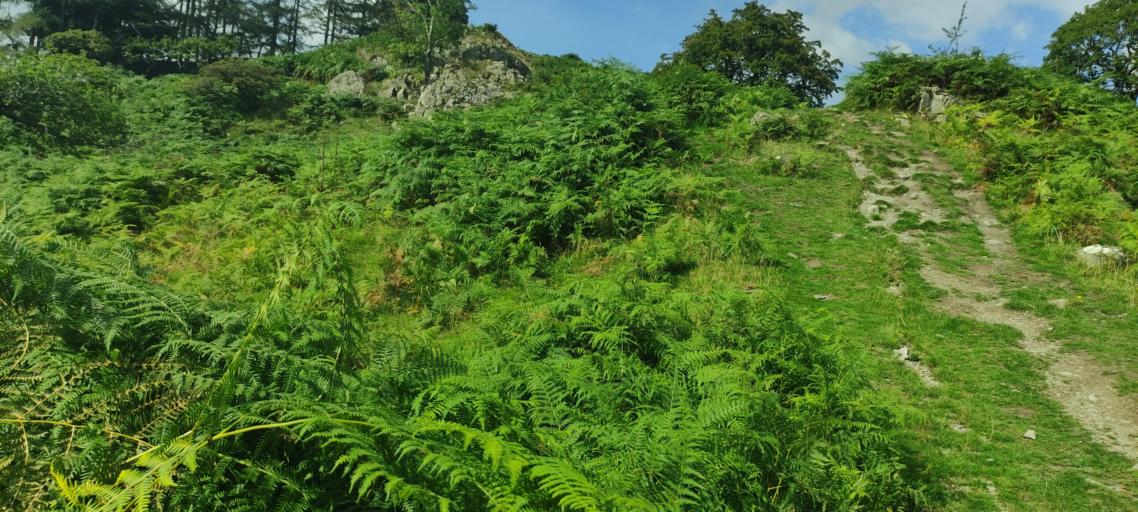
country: GB
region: England
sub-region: Cumbria
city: Ambleside
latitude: 54.4459
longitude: -2.9627
